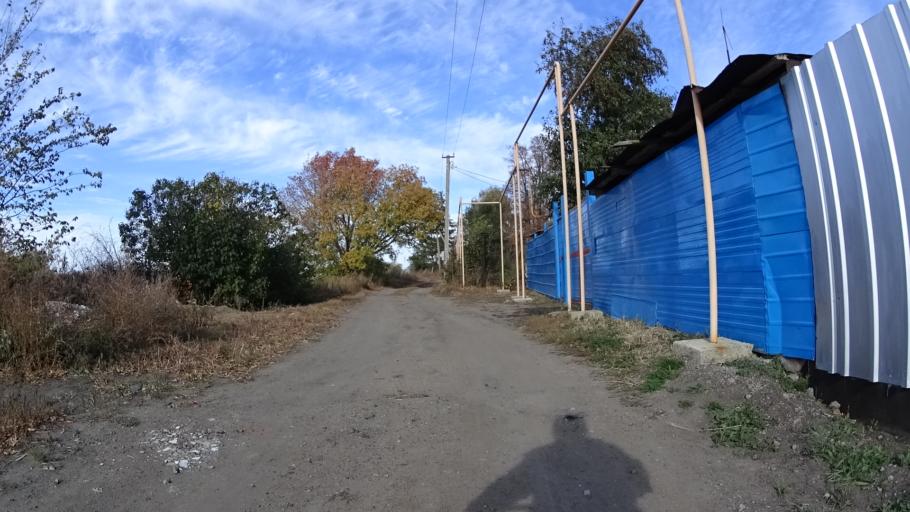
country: RU
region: Chelyabinsk
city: Troitsk
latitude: 54.0733
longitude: 61.5820
